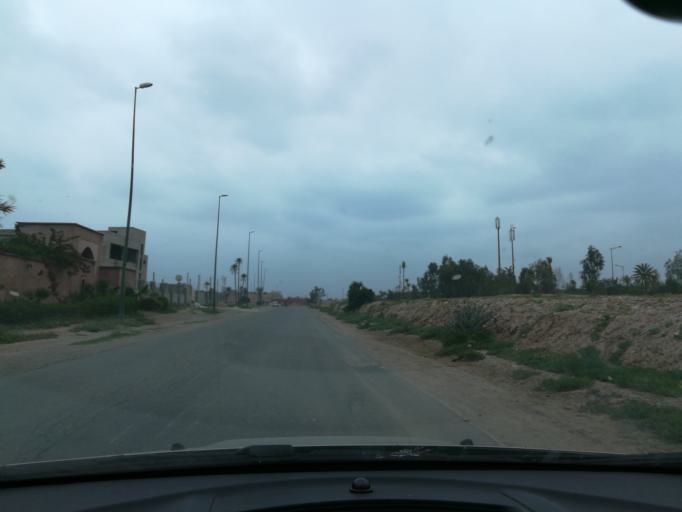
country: MA
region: Marrakech-Tensift-Al Haouz
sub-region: Marrakech
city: Marrakesh
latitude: 31.6531
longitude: -7.9848
